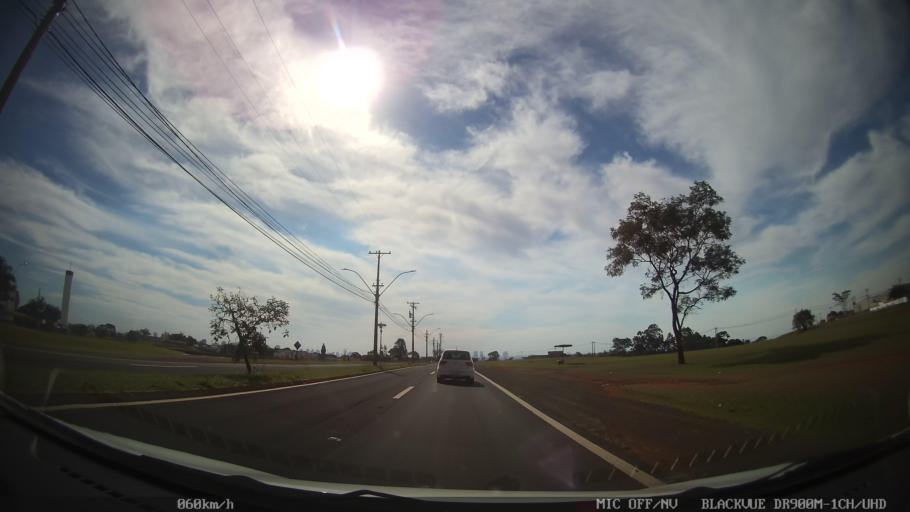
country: BR
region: Sao Paulo
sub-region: Araraquara
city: Araraquara
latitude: -21.8144
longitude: -48.1579
